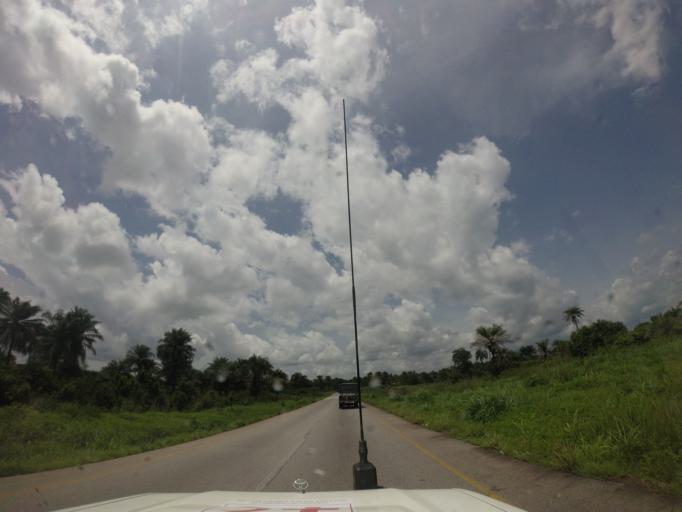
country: SL
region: Northern Province
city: Rokupr
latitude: 8.4820
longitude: -12.4480
